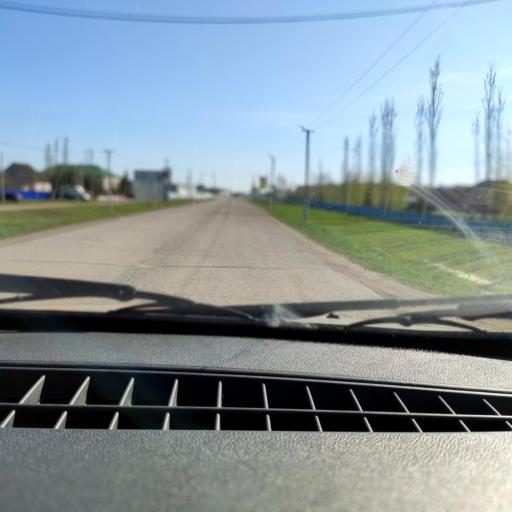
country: RU
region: Bashkortostan
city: Kabakovo
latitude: 54.6004
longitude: 56.1835
